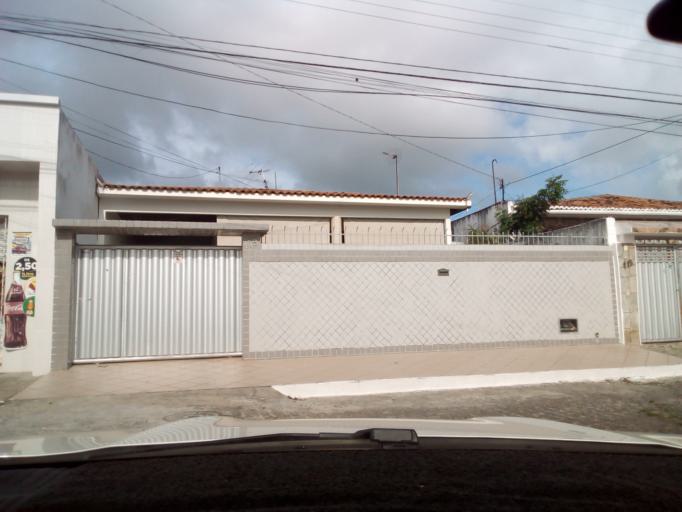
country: BR
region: Paraiba
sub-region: Joao Pessoa
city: Joao Pessoa
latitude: -7.1745
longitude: -34.8425
